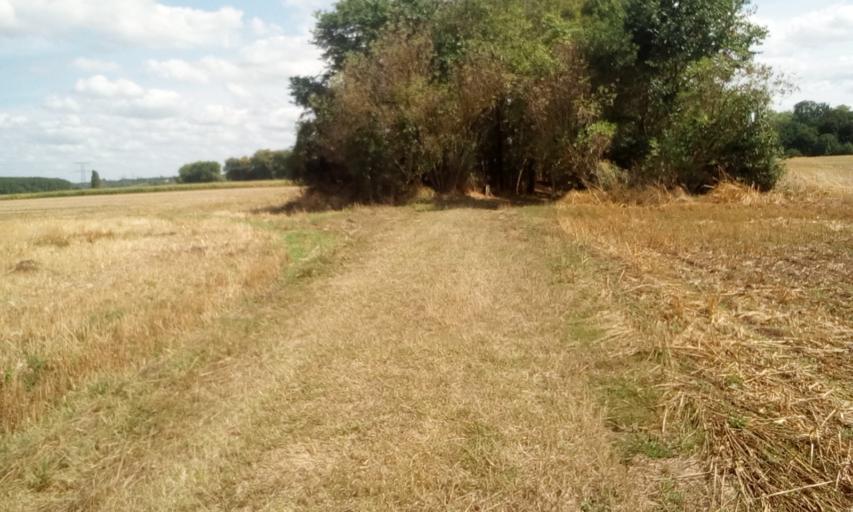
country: FR
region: Lower Normandy
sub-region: Departement du Calvados
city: Bellengreville
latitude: 49.1310
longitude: -0.2008
